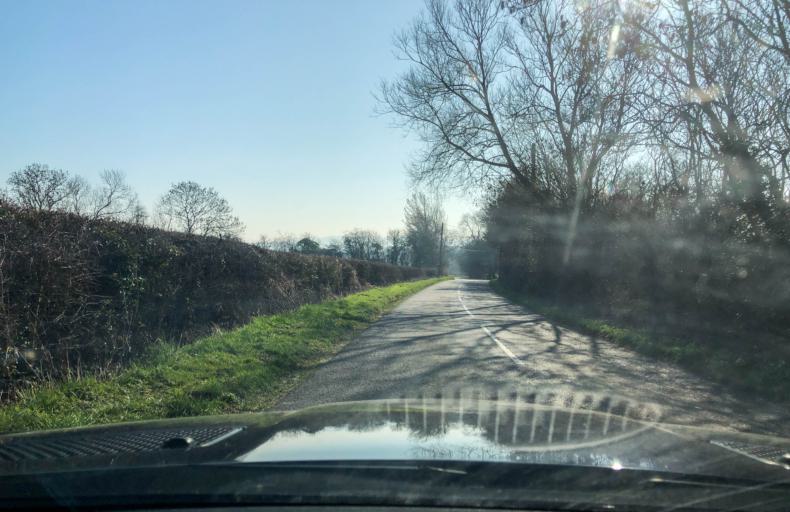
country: GB
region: England
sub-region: Warwickshire
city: Wellesbourne Mountford
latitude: 52.1652
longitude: -1.5150
